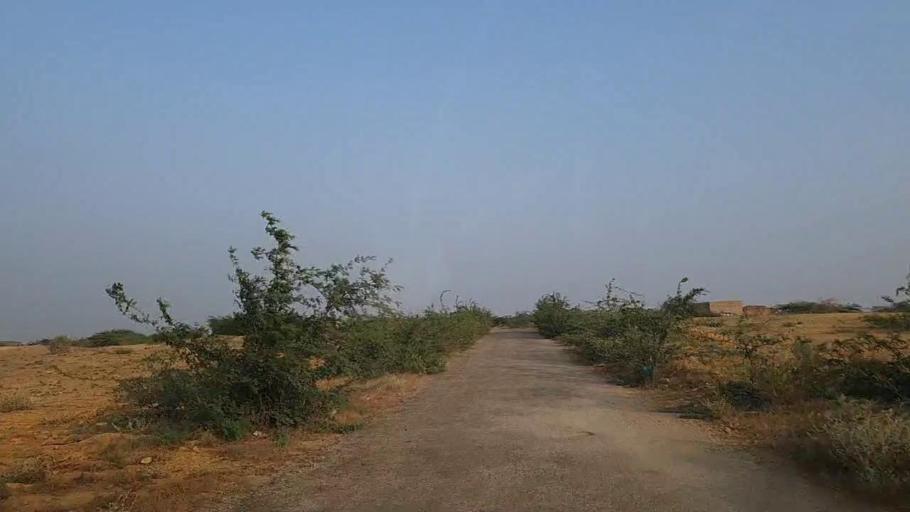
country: PK
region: Sindh
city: Thatta
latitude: 24.6900
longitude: 67.8244
